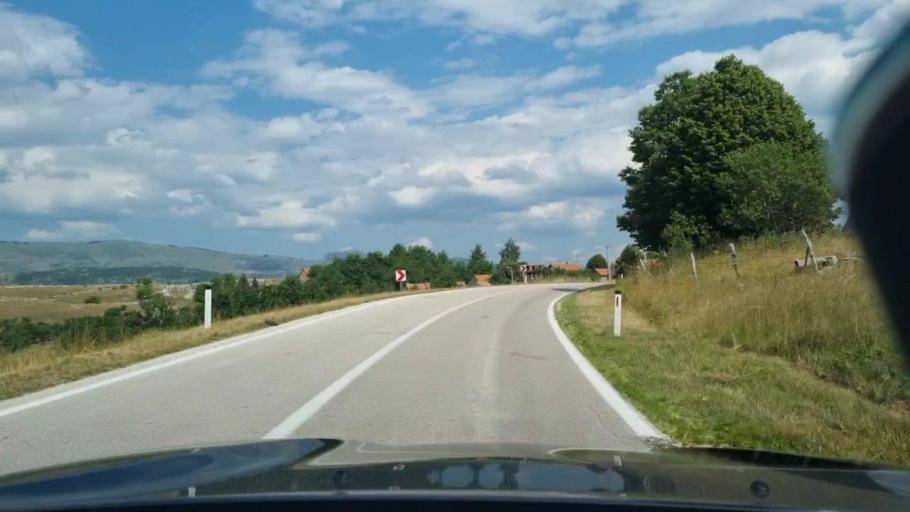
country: BA
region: Federation of Bosnia and Herzegovina
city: Bosansko Grahovo
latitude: 44.1582
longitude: 16.4048
